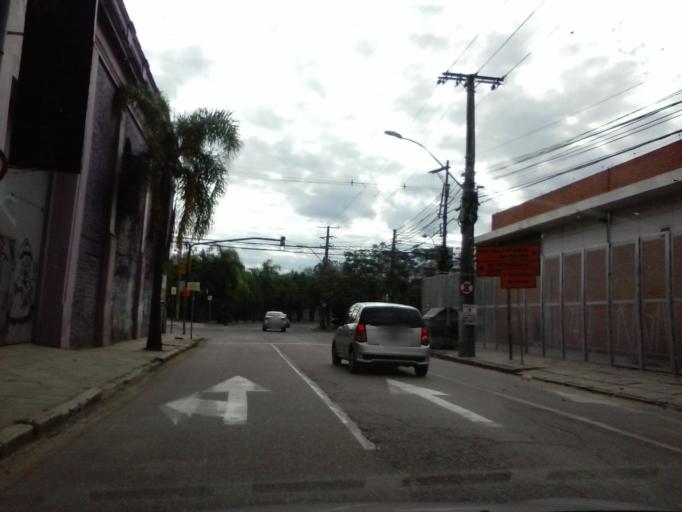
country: BR
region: Rio Grande do Sul
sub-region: Porto Alegre
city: Porto Alegre
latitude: -30.0208
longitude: -51.2143
